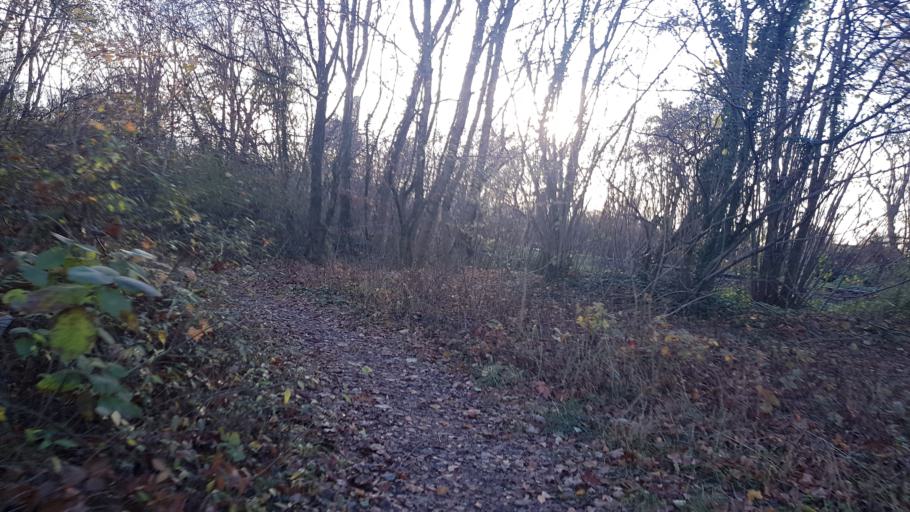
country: DE
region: Bavaria
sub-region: Upper Bavaria
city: Oberschleissheim
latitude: 48.2058
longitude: 11.5409
